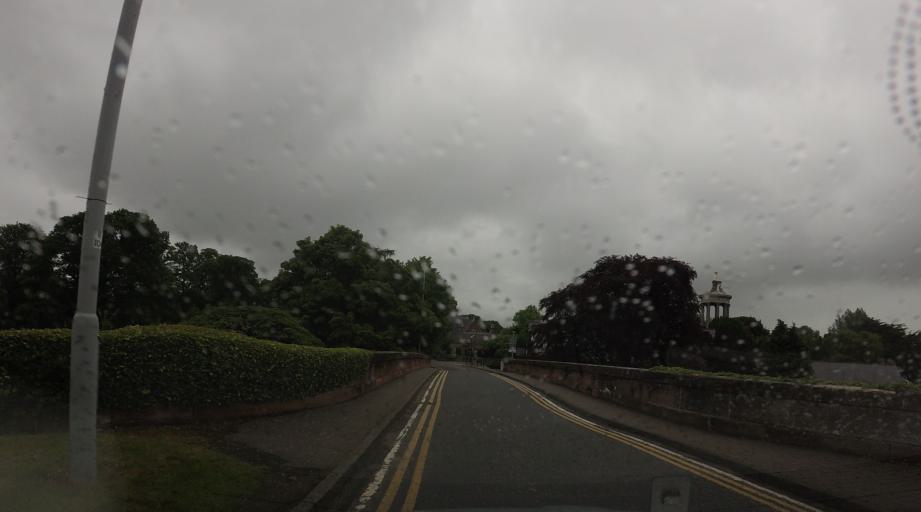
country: GB
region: Scotland
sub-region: South Ayrshire
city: Ayr
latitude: 55.4268
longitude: -4.6385
